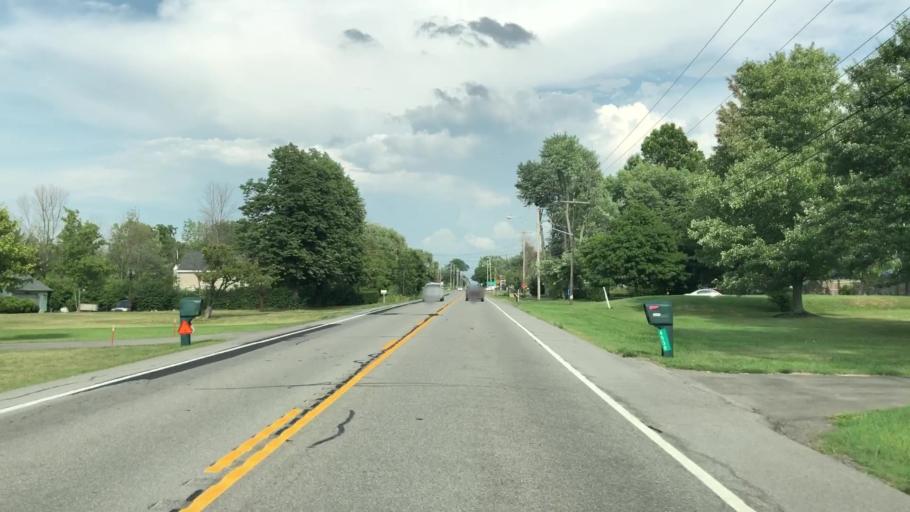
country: US
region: New York
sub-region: Erie County
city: Elma Center
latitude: 42.8556
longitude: -78.6442
